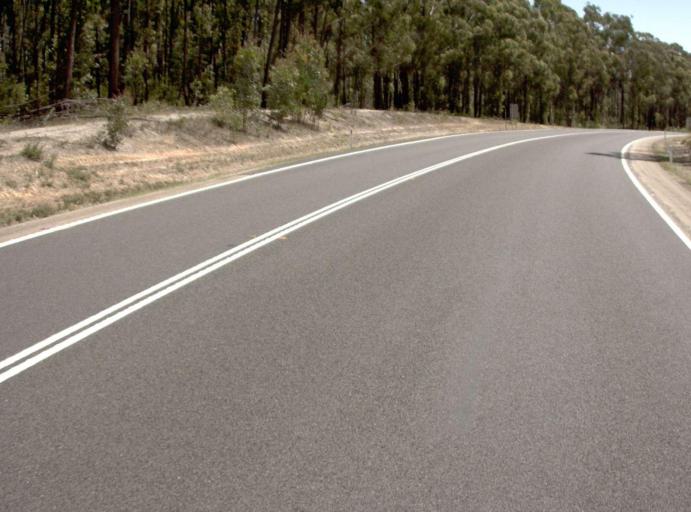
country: AU
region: New South Wales
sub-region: Bombala
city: Bombala
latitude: -37.5672
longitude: 149.1122
